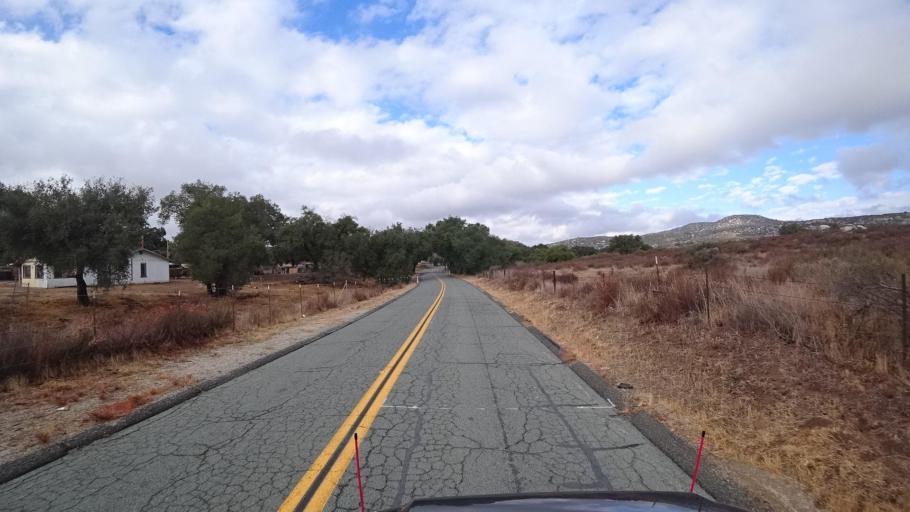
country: MX
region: Baja California
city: Tecate
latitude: 32.6264
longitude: -116.5965
